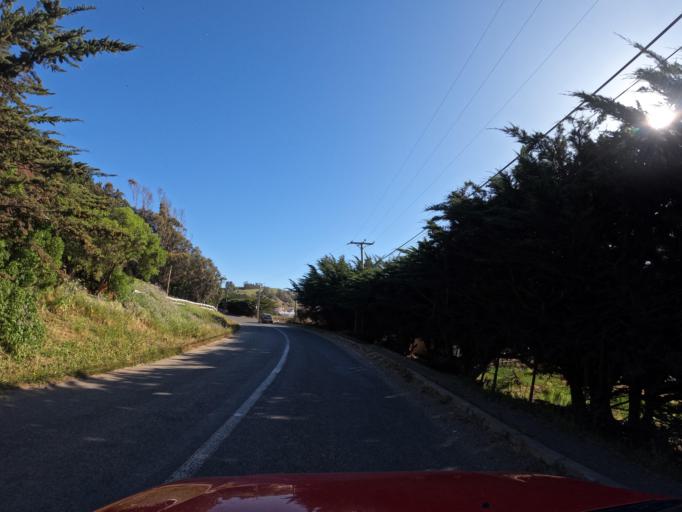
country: CL
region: Maule
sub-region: Provincia de Talca
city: Constitucion
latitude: -34.8776
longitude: -72.1552
